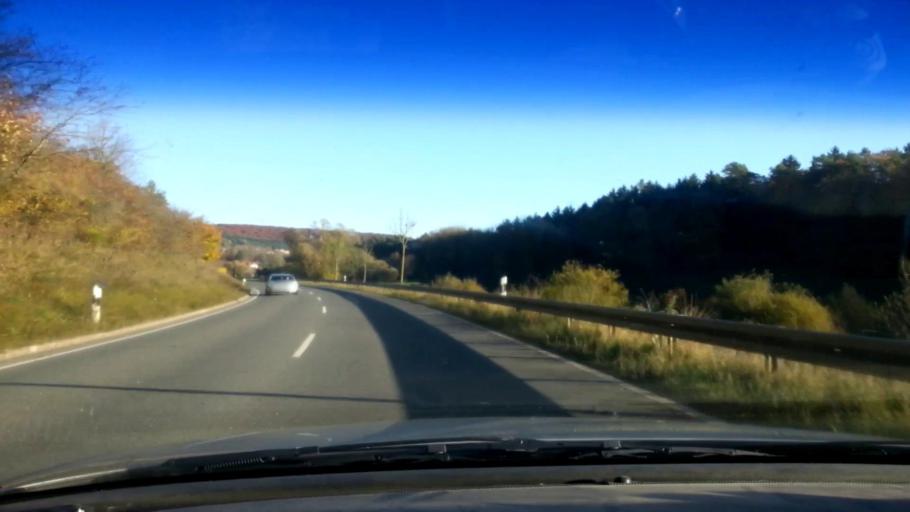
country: DE
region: Bavaria
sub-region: Upper Franconia
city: Heiligenstadt
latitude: 49.8684
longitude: 11.1583
